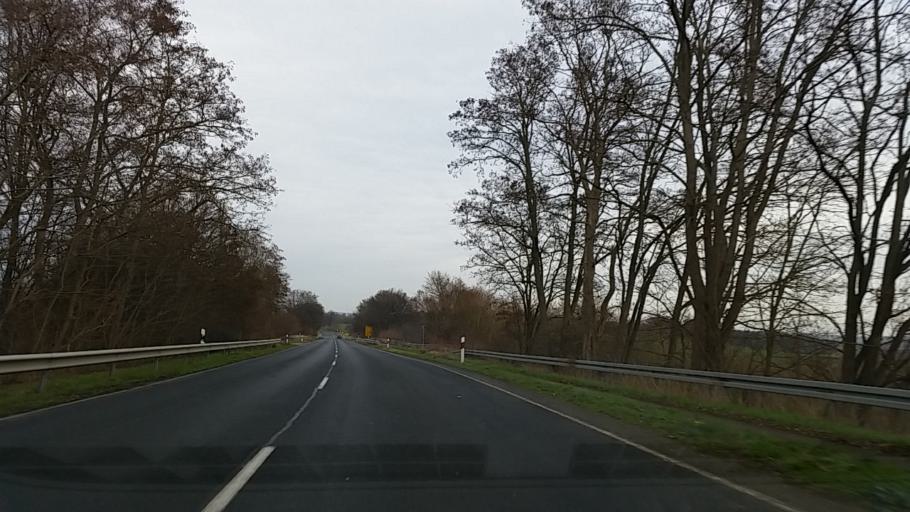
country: DE
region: Lower Saxony
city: Liebenburg
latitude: 52.0597
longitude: 10.3989
